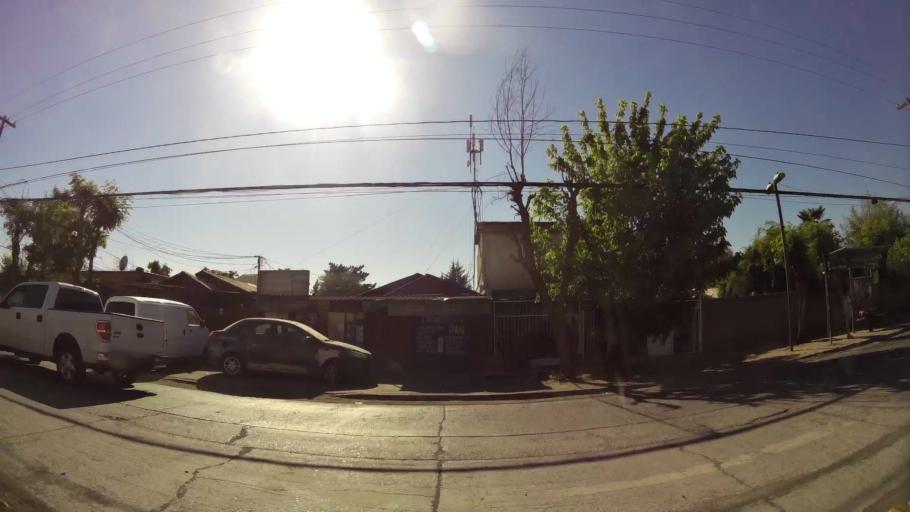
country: CL
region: Santiago Metropolitan
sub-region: Provincia de Maipo
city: San Bernardo
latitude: -33.5531
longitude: -70.6917
